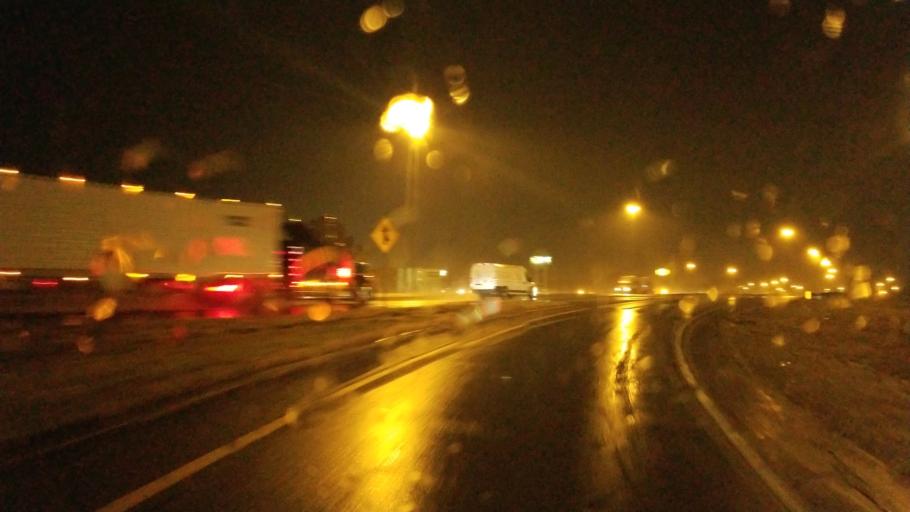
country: US
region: Ohio
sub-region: Trumbull County
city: Churchill
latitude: 41.1570
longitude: -80.6631
